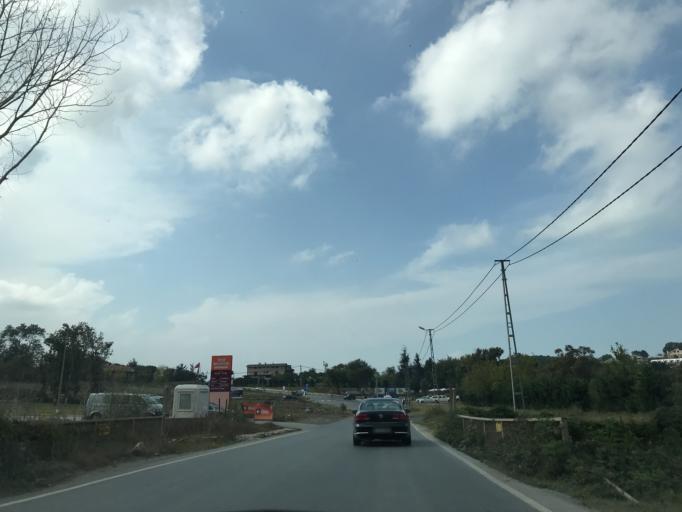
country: TR
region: Istanbul
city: Arikoey
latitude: 41.2189
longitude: 29.0343
